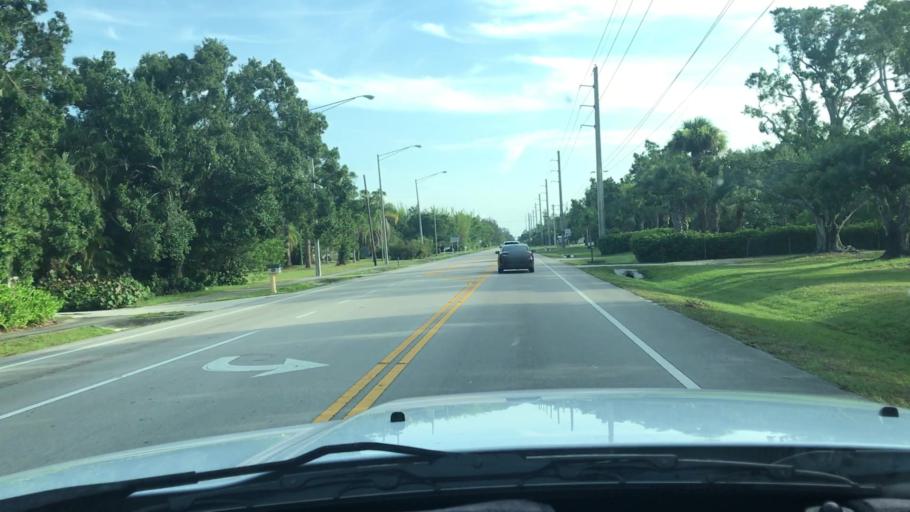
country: US
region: Florida
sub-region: Indian River County
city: Vero Beach South
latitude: 27.6168
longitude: -80.4139
